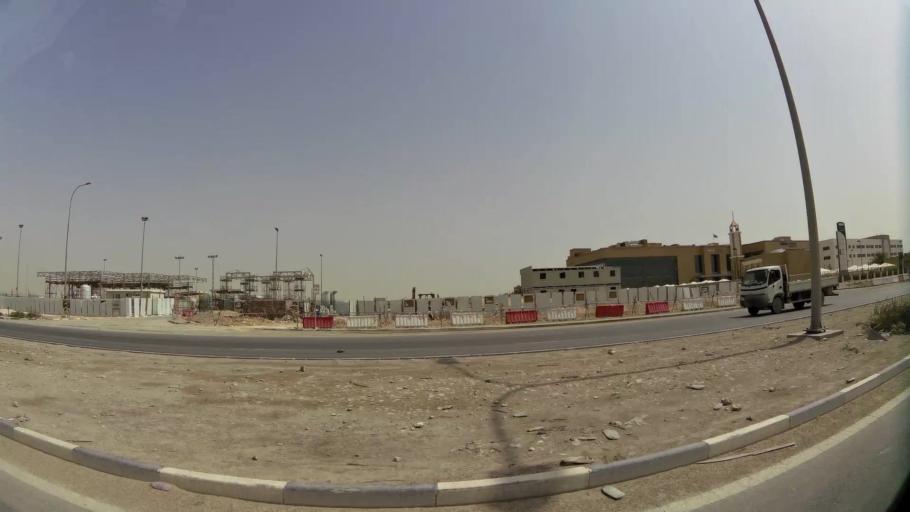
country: QA
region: Baladiyat ar Rayyan
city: Ar Rayyan
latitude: 25.1670
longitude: 51.4027
